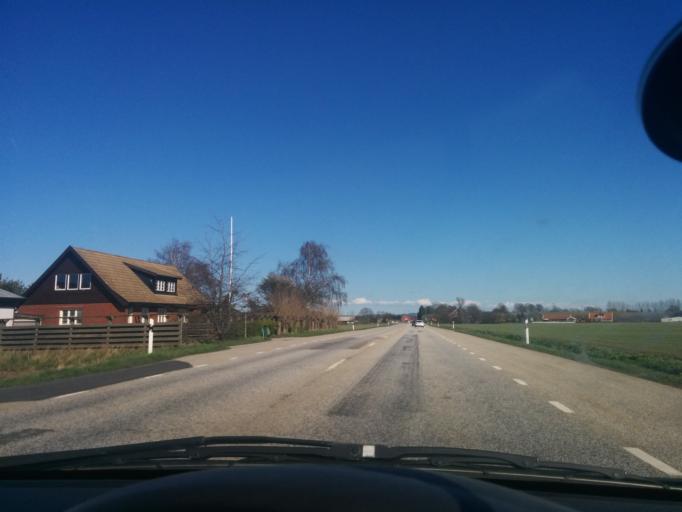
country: SE
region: Skane
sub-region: Staffanstorps Kommun
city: Hjaerup
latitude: 55.6426
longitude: 13.1412
